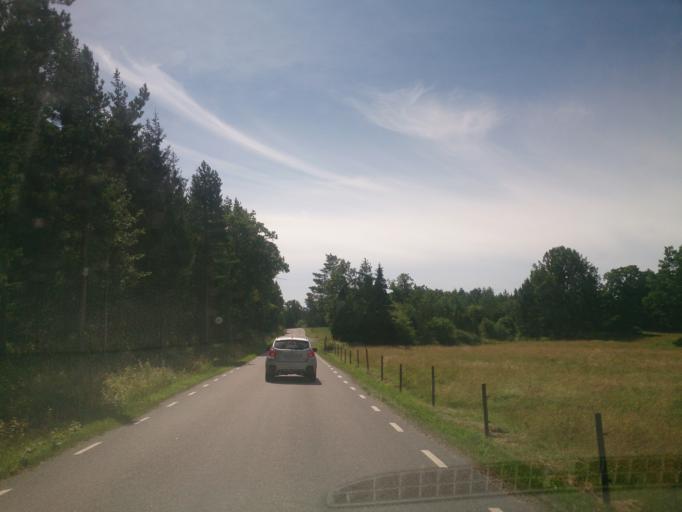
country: SE
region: OEstergoetland
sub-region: Valdemarsviks Kommun
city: Valdemarsvik
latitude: 58.2742
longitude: 16.7067
